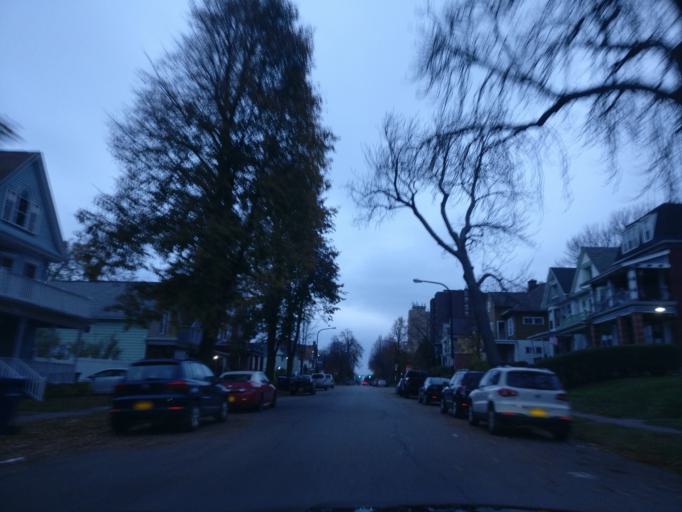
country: US
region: New York
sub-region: Erie County
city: Buffalo
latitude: 42.8996
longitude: -78.8889
